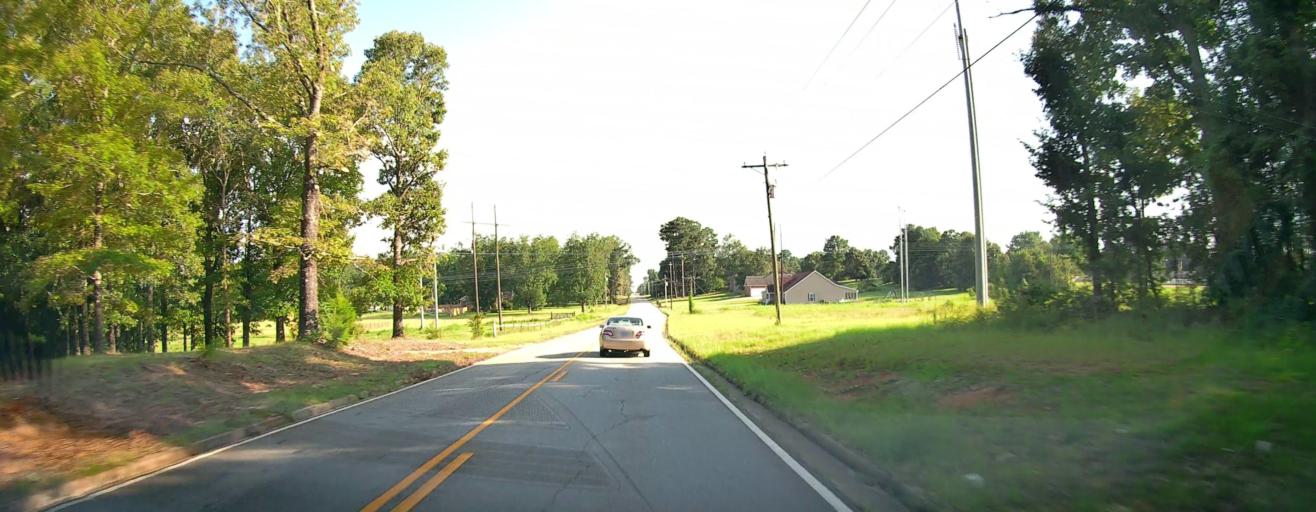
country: US
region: Georgia
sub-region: Houston County
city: Robins Air Force Base
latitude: 32.5663
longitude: -83.6044
